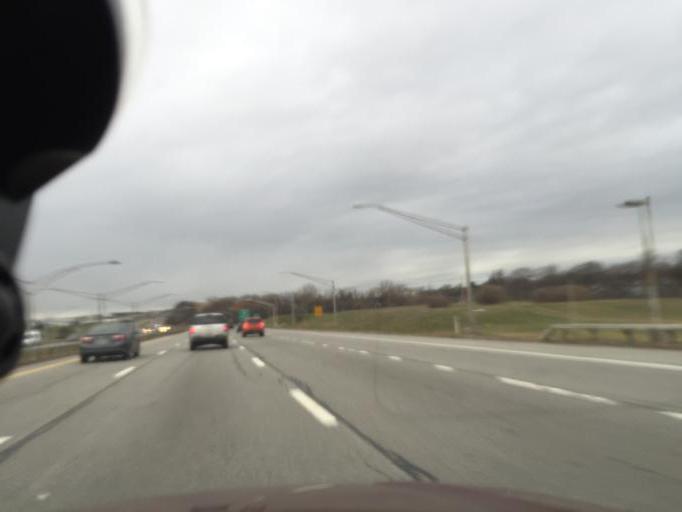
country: US
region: New York
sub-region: Monroe County
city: Rochester
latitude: 43.1225
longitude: -77.6477
